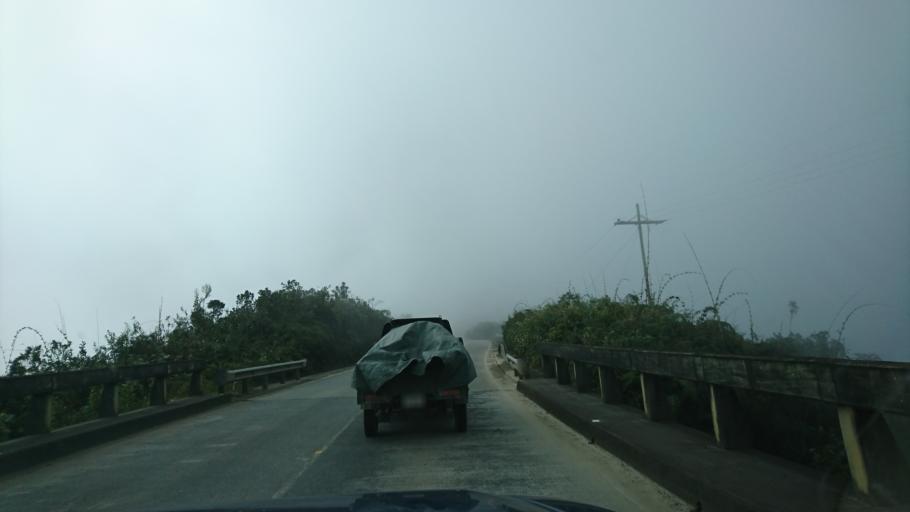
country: BO
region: La Paz
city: Coroico
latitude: -16.2432
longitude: -67.8332
